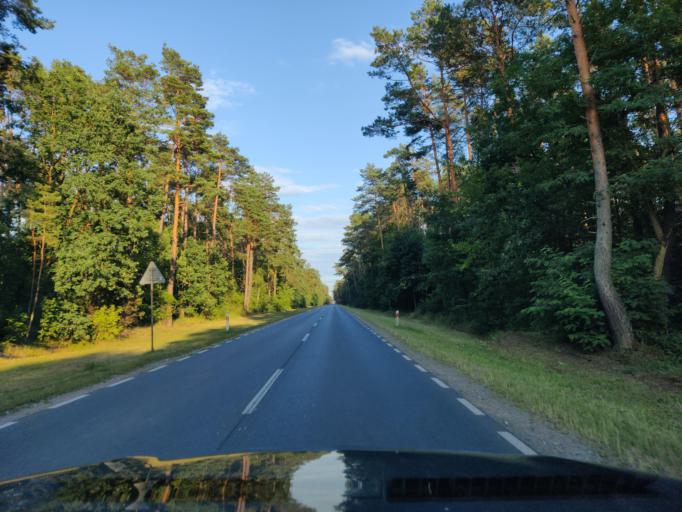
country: PL
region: Masovian Voivodeship
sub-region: Powiat pultuski
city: Pultusk
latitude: 52.6803
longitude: 21.1314
